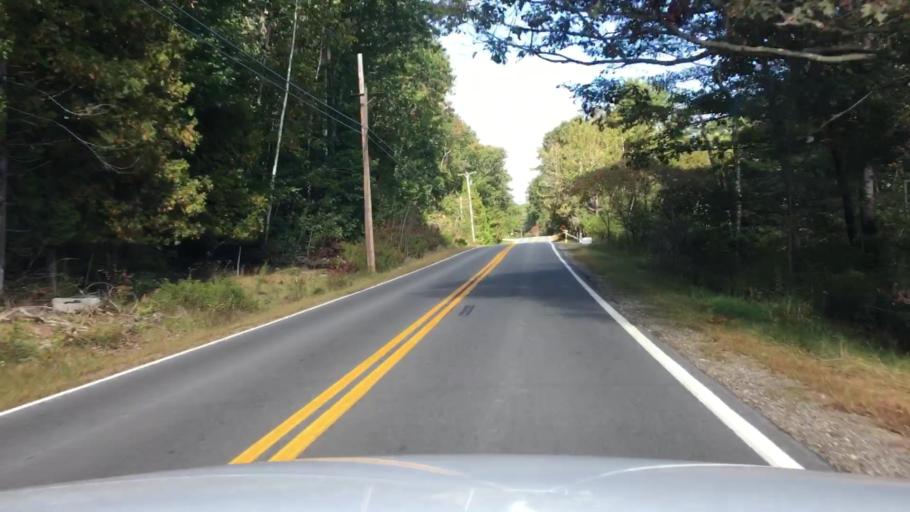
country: US
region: Maine
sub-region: Sagadahoc County
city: North Bath
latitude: 43.9909
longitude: -69.8903
